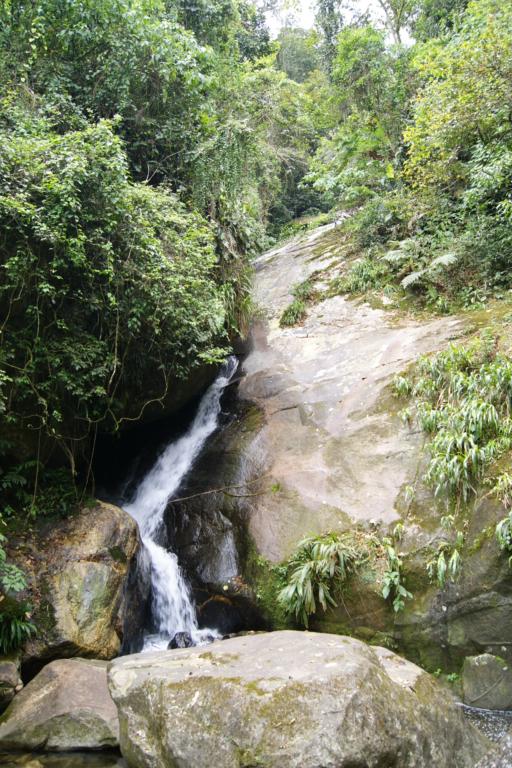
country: BR
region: Sao Paulo
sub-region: Rio Grande Da Serra
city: Rio Grande da Serra
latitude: -23.8056
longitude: -46.2980
